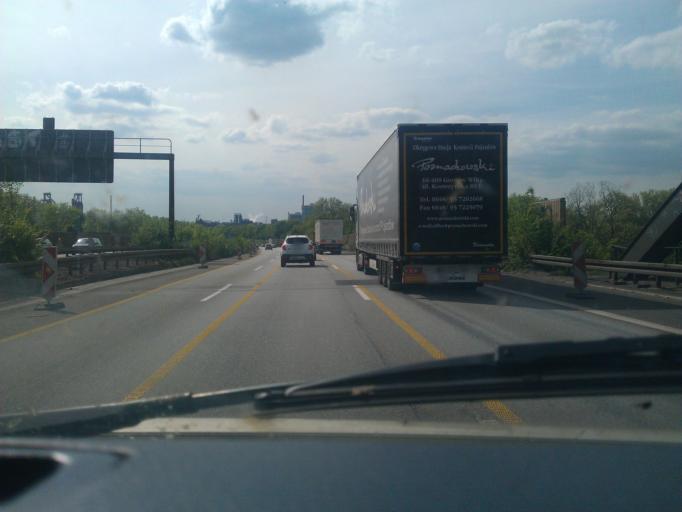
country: DE
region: North Rhine-Westphalia
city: Meiderich
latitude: 51.4869
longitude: 6.7586
